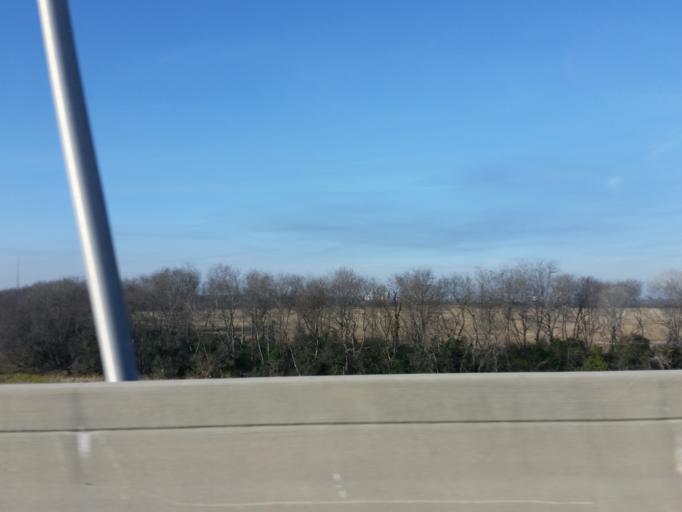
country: US
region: South Carolina
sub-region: Charleston County
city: Charleston
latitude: 32.8049
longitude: -79.9382
